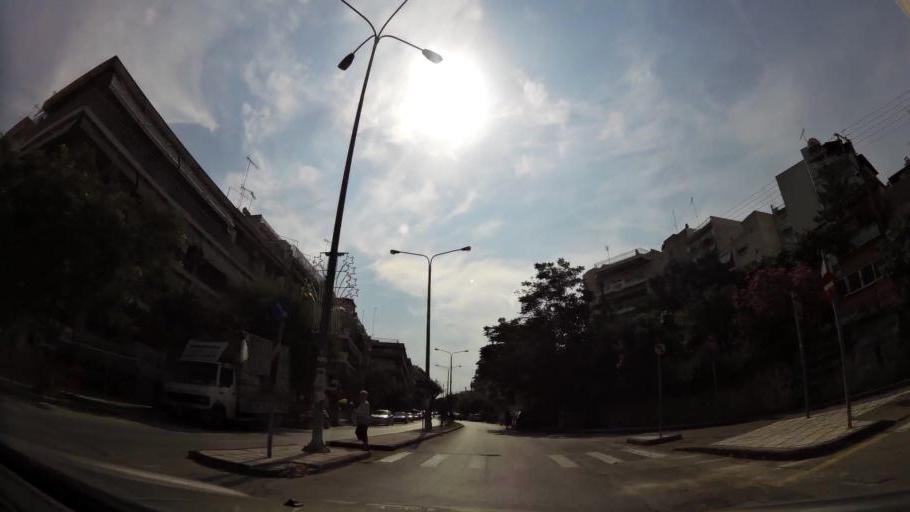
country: GR
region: Central Macedonia
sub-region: Nomos Thessalonikis
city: Sykies
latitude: 40.6509
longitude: 22.9546
